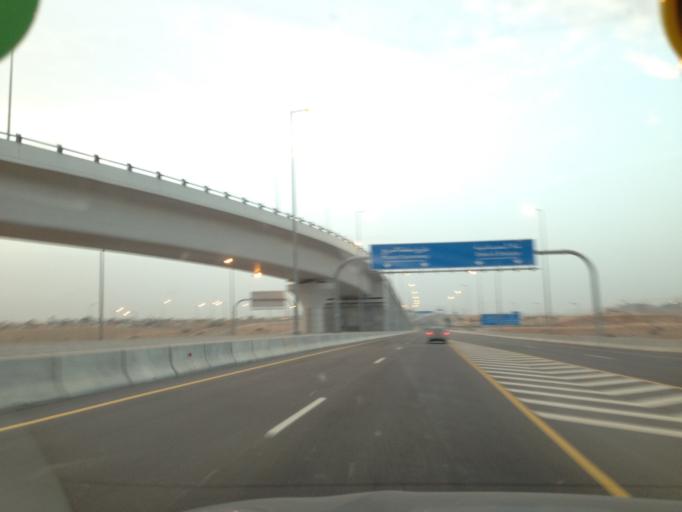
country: OM
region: Muhafazat Masqat
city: Bawshar
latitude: 23.5825
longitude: 58.3326
